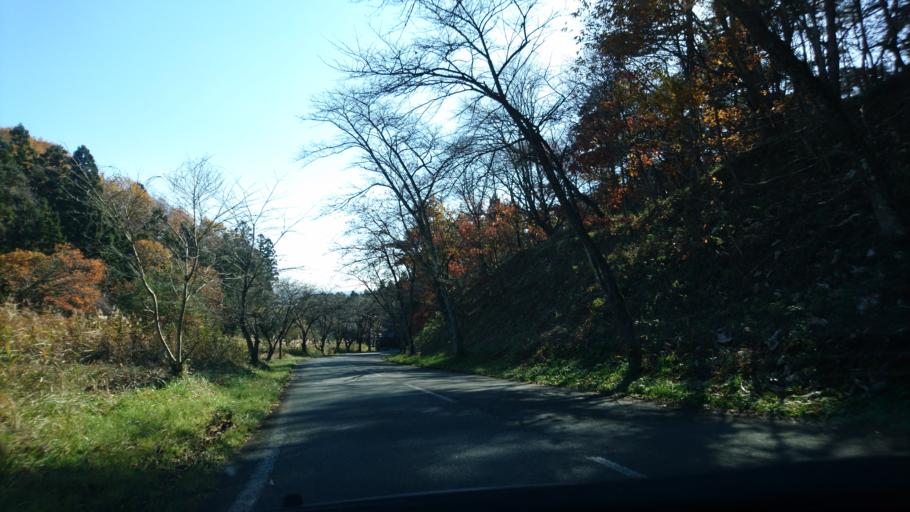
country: JP
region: Iwate
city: Ichinoseki
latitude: 38.9916
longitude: 141.1076
